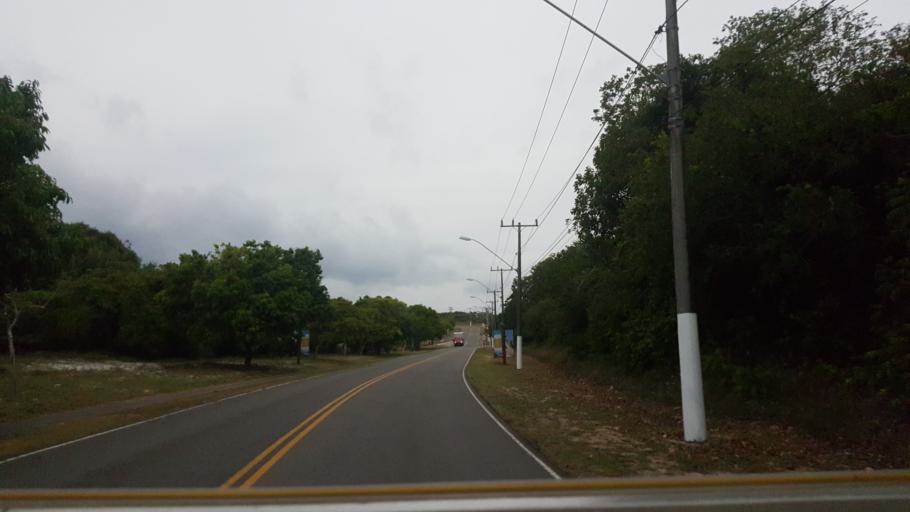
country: BR
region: Bahia
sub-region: Mata De Sao Joao
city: Mata de Sao Joao
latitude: -12.4269
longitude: -37.9222
